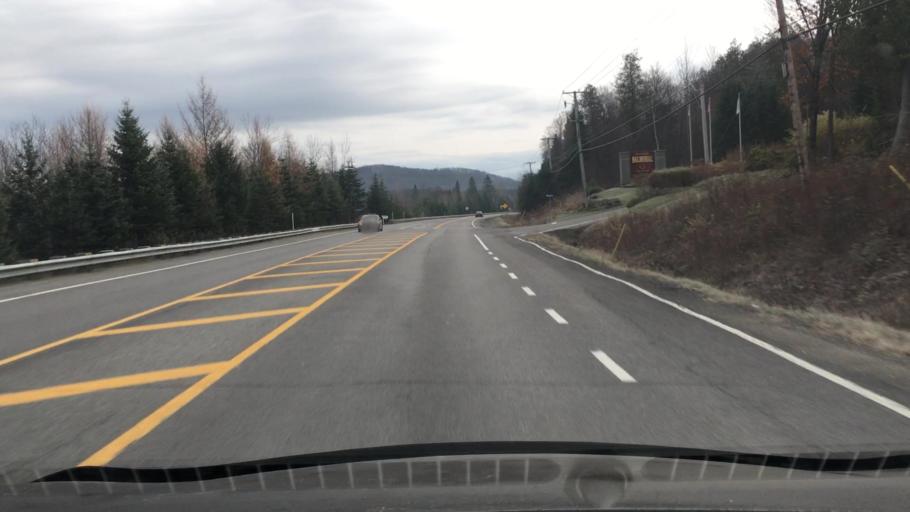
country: CA
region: Quebec
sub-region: Laurentides
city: Saint-Sauveur
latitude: 45.8999
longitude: -74.2192
